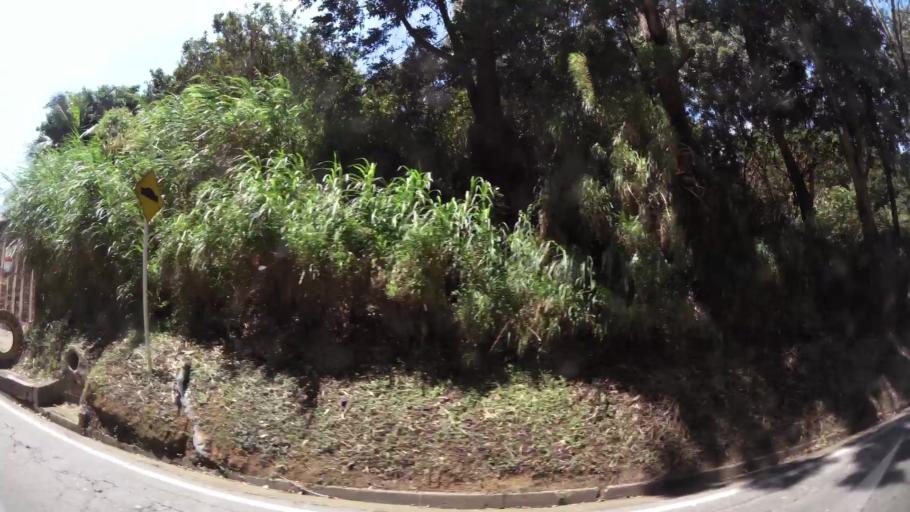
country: CO
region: Antioquia
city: La Estrella
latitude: 6.1843
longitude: -75.6515
